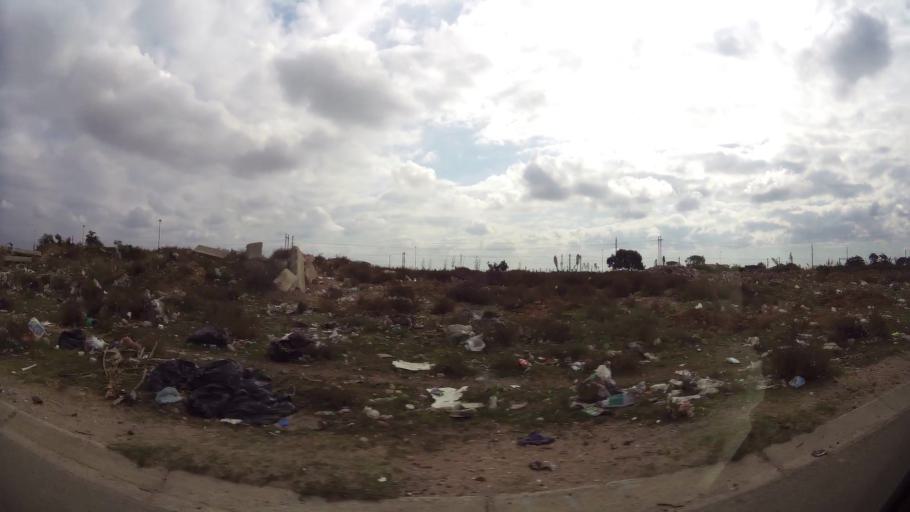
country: ZA
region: Eastern Cape
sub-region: Nelson Mandela Bay Metropolitan Municipality
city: Port Elizabeth
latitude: -33.8208
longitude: 25.6279
